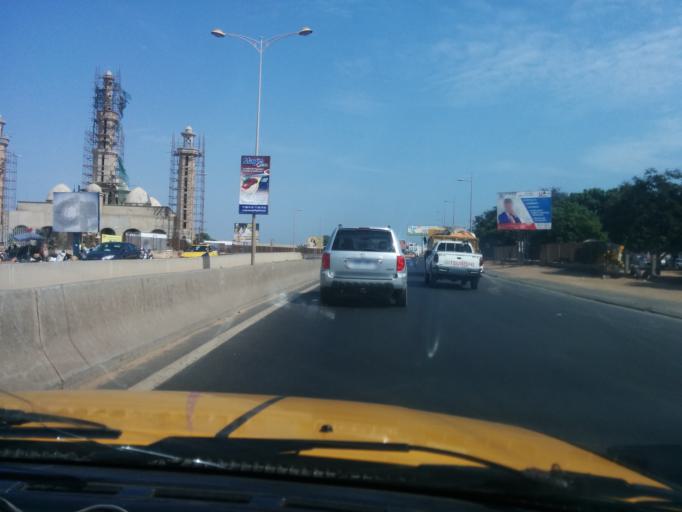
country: SN
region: Dakar
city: Grand Dakar
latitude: 14.7430
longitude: -17.4427
